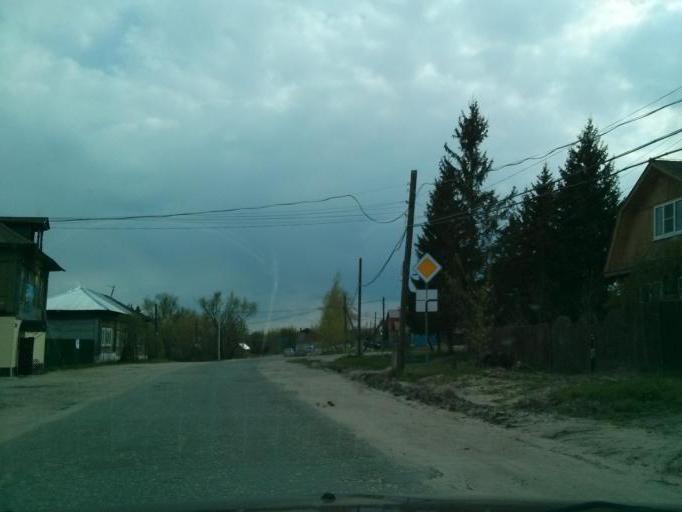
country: RU
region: Nizjnij Novgorod
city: Shimorskoye
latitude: 55.3348
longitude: 41.9282
